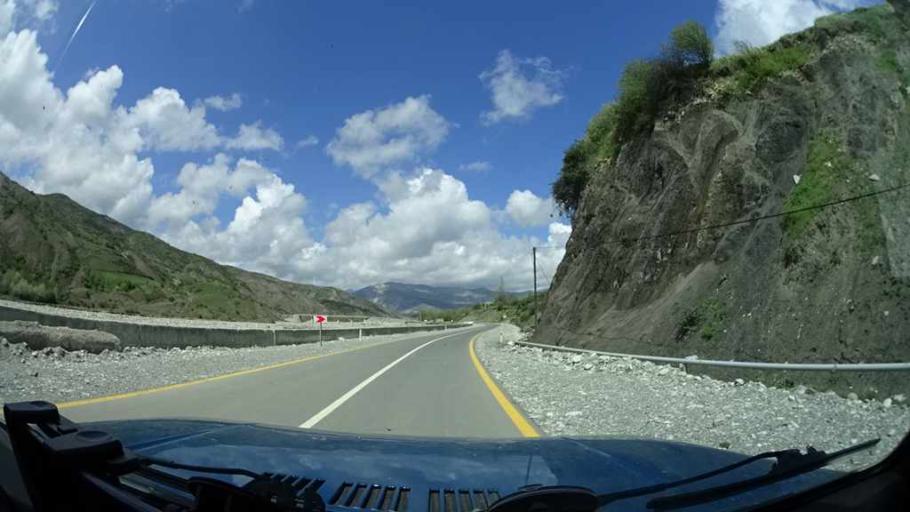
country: AZ
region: Ismayilli
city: Basqal
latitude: 40.8475
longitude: 48.3814
